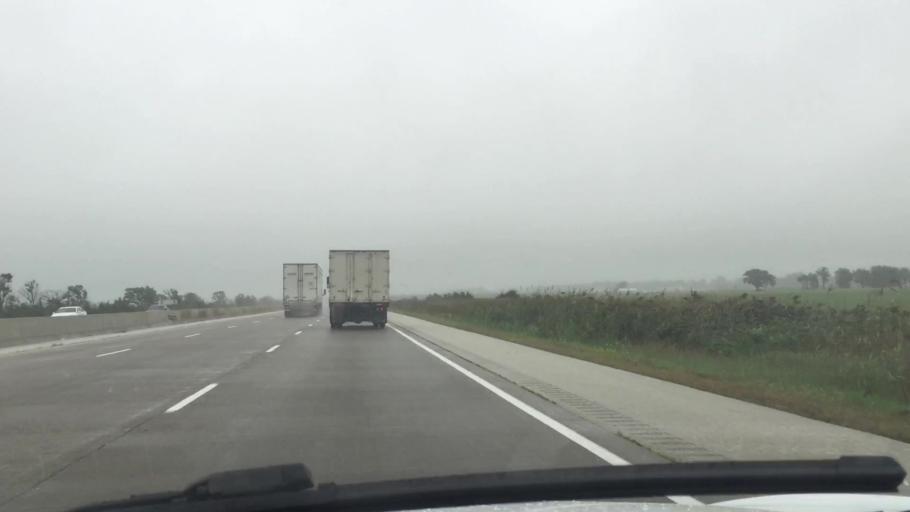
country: US
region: Michigan
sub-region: Wayne County
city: Grosse Pointe Farms
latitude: 42.2428
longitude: -82.5659
